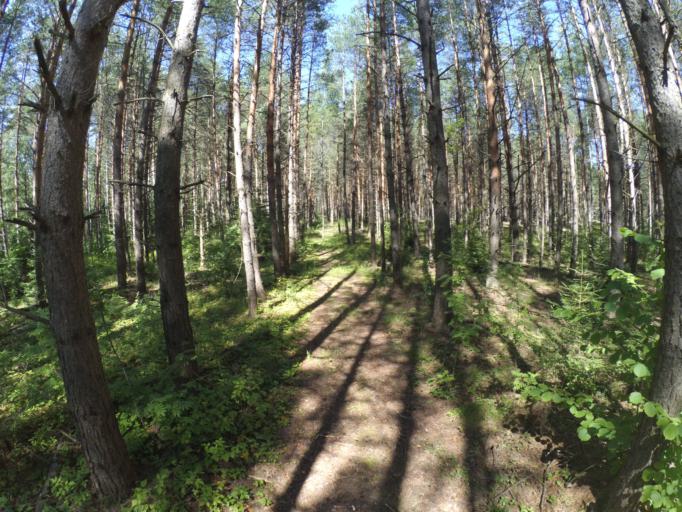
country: RU
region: Moskovskaya
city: Fosforitnyy
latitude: 55.3415
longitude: 38.9222
